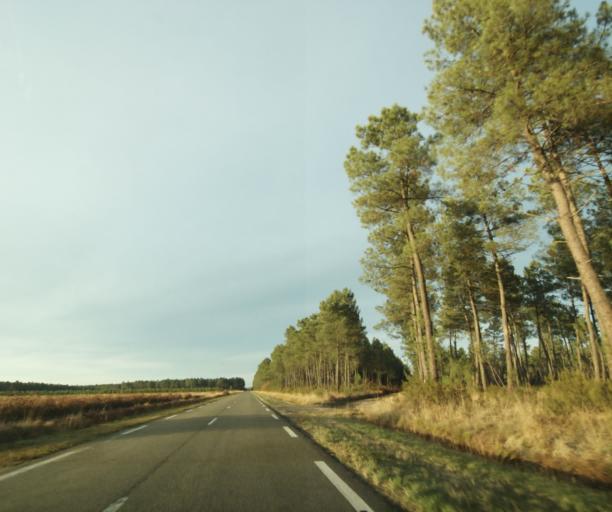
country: FR
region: Aquitaine
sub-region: Departement des Landes
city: Roquefort
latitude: 44.1720
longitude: -0.1403
